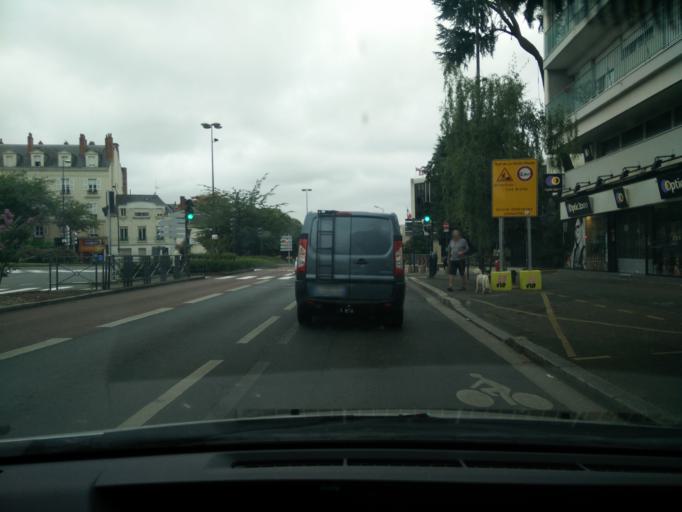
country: FR
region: Pays de la Loire
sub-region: Departement de Maine-et-Loire
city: Angers
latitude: 47.4736
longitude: -0.5445
